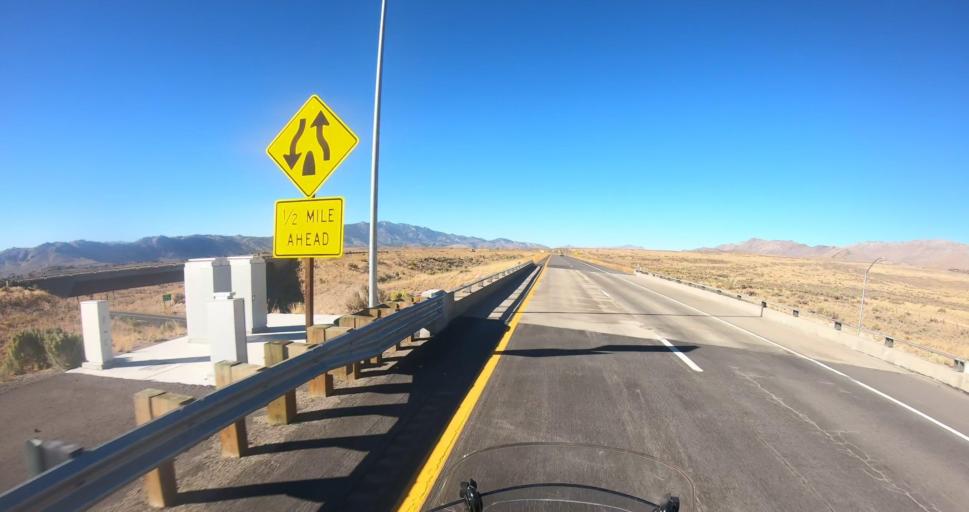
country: US
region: Nevada
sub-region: Washoe County
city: Cold Springs
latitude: 39.7747
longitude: -120.0384
